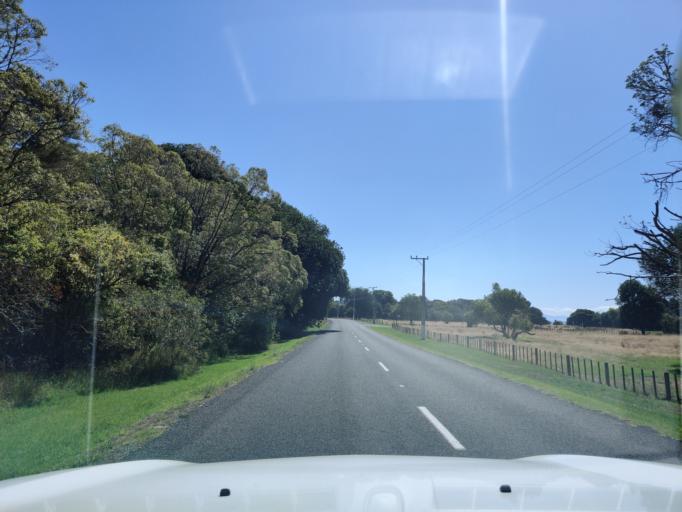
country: NZ
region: Waikato
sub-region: Thames-Coromandel District
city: Thames
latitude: -37.0408
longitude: 175.2953
